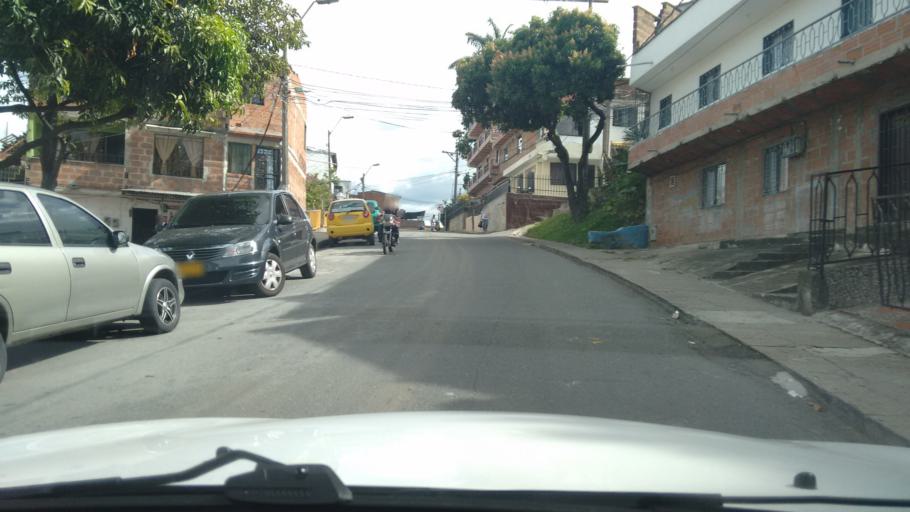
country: CO
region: Antioquia
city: Bello
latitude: 6.2987
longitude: -75.5774
